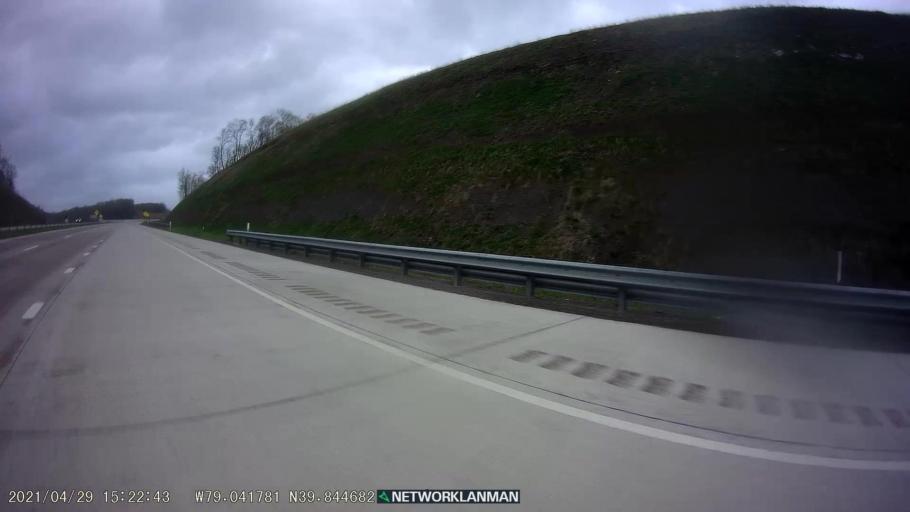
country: US
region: Pennsylvania
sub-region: Somerset County
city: Meyersdale
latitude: 39.8452
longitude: -79.0418
